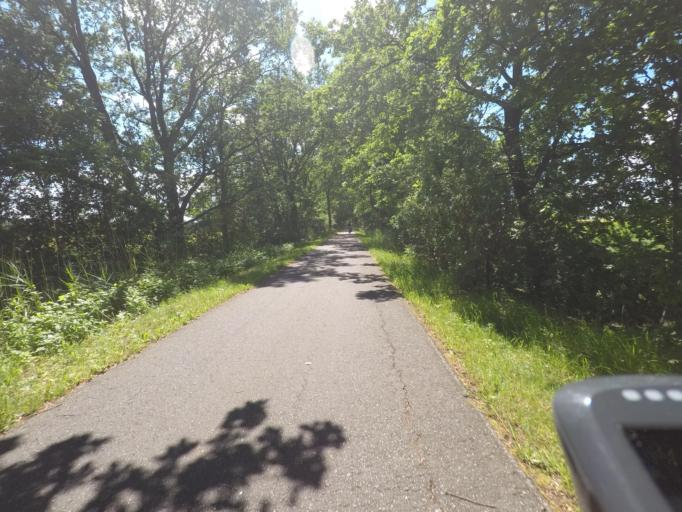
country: DE
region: Hamburg
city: Bergedorf
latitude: 53.4339
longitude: 10.2098
